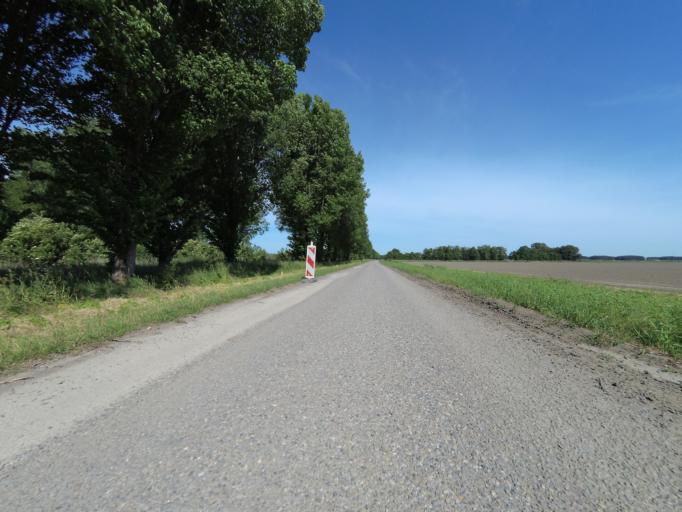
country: NL
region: Utrecht
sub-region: Gemeente Bunschoten
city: Spakenburg
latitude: 52.3355
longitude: 5.3387
